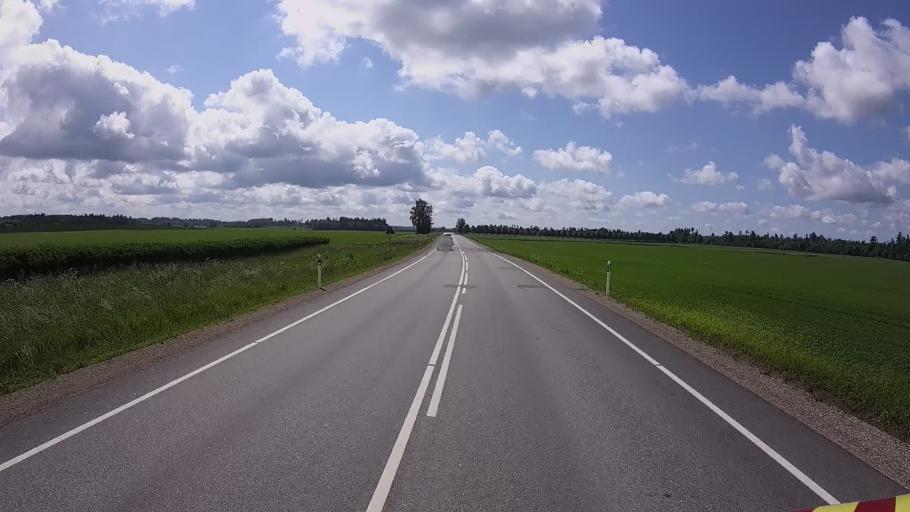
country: EE
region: Viljandimaa
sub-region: Viiratsi vald
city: Viiratsi
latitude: 58.3519
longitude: 25.6255
